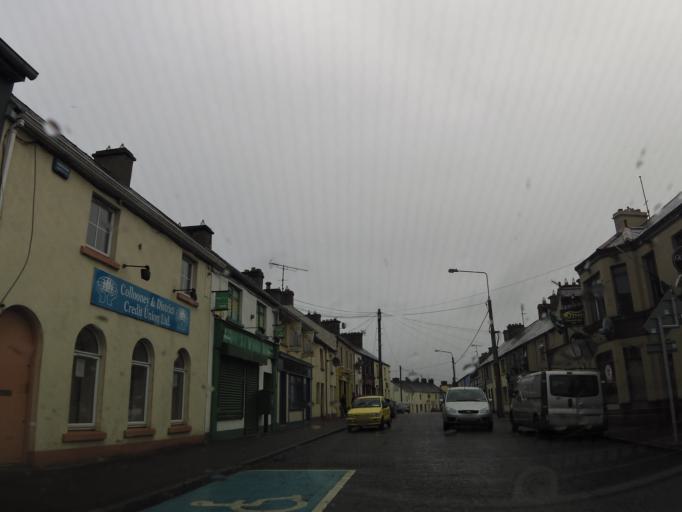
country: IE
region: Connaught
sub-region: Sligo
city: Collooney
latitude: 54.1841
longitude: -8.4928
